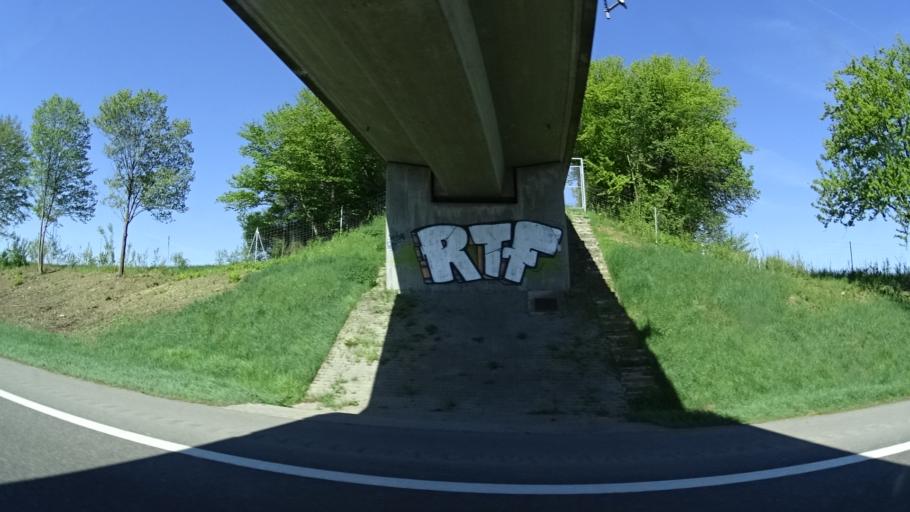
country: DE
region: Baden-Wuerttemberg
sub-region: Freiburg Region
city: Muhlheim am Bach
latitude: 48.3641
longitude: 8.6870
